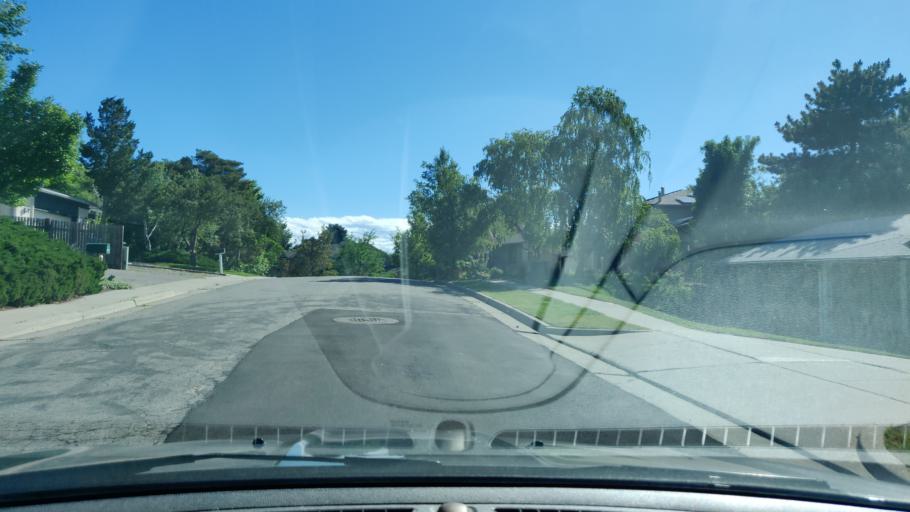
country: US
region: Utah
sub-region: Salt Lake County
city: Cottonwood Heights
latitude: 40.6143
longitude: -111.8095
